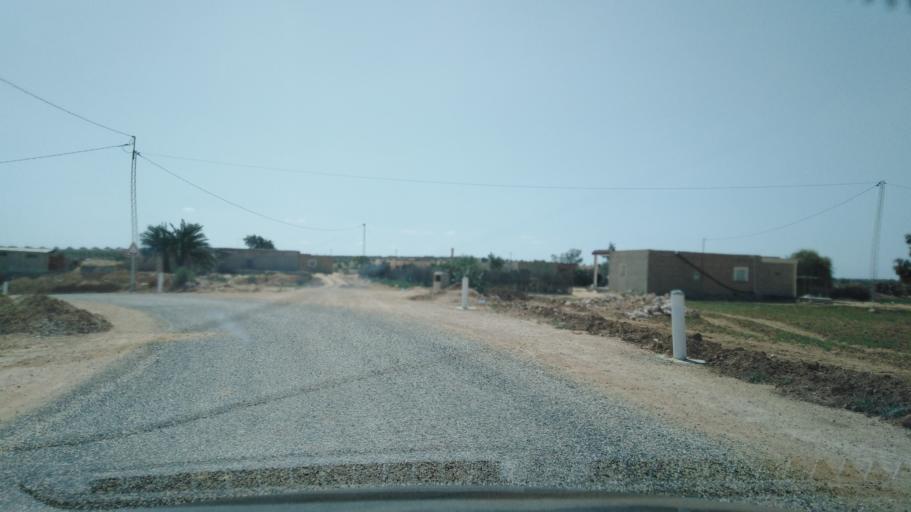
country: TN
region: Safaqis
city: Sfax
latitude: 34.6885
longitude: 10.4475
